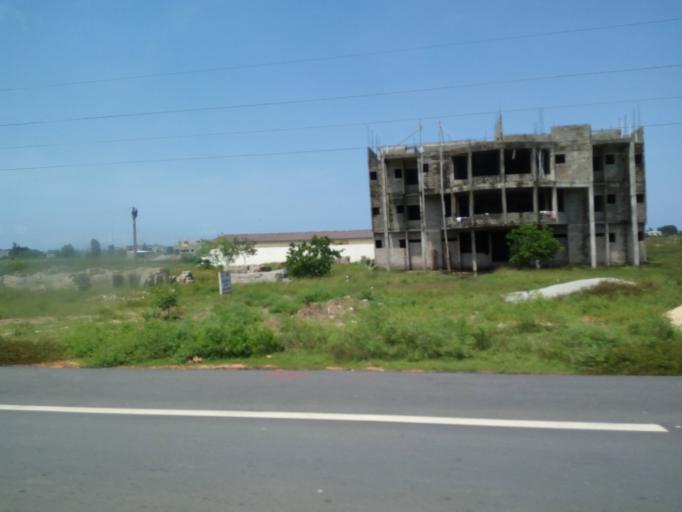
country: CI
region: Sud-Comoe
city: Grand-Bassam
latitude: 5.2281
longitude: -3.7459
